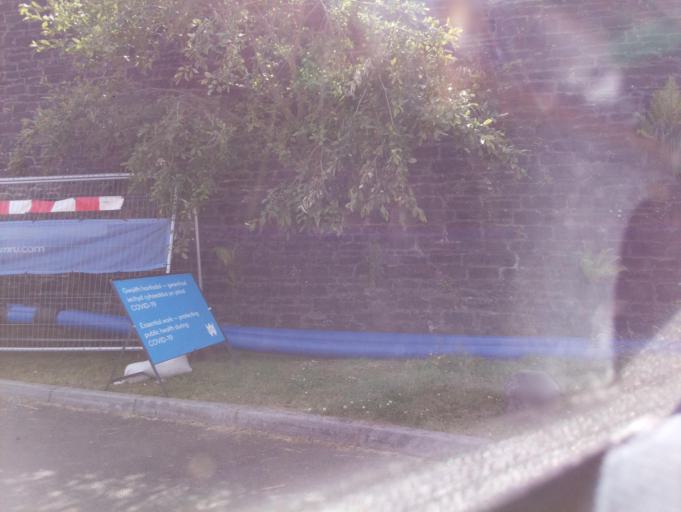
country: GB
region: Wales
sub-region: Caerphilly County Borough
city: New Tredegar
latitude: 51.7231
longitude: -3.2507
